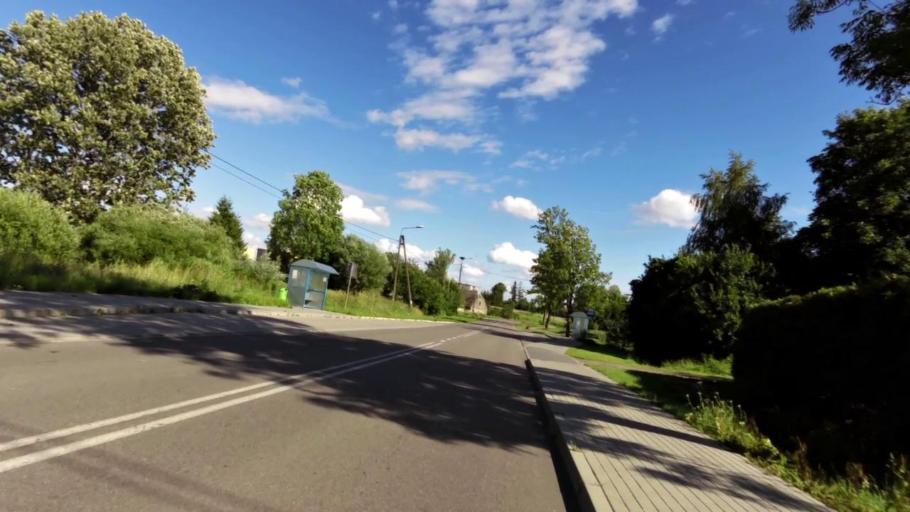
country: PL
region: West Pomeranian Voivodeship
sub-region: Powiat slawienski
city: Slawno
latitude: 54.4591
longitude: 16.7364
